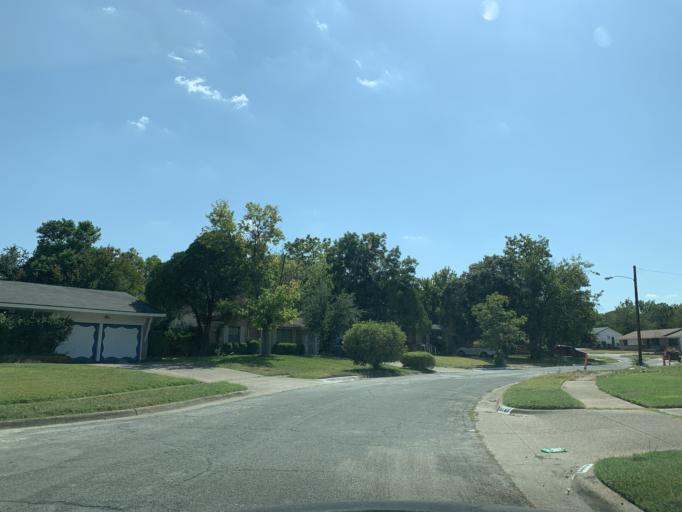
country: US
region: Texas
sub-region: Dallas County
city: Hutchins
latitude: 32.6778
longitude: -96.7948
